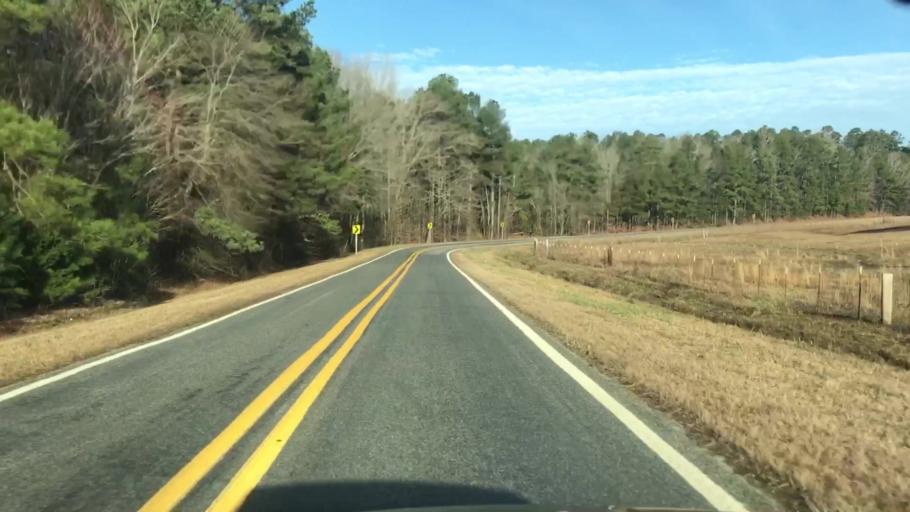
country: US
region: Arkansas
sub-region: Garland County
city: Rockwell
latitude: 34.4804
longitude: -93.2723
